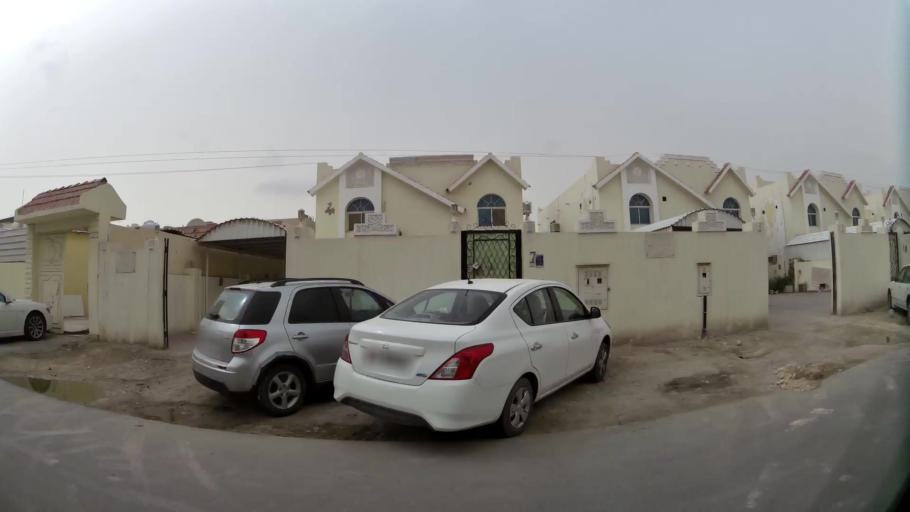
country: QA
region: Baladiyat ad Dawhah
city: Doha
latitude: 25.2420
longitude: 51.5197
